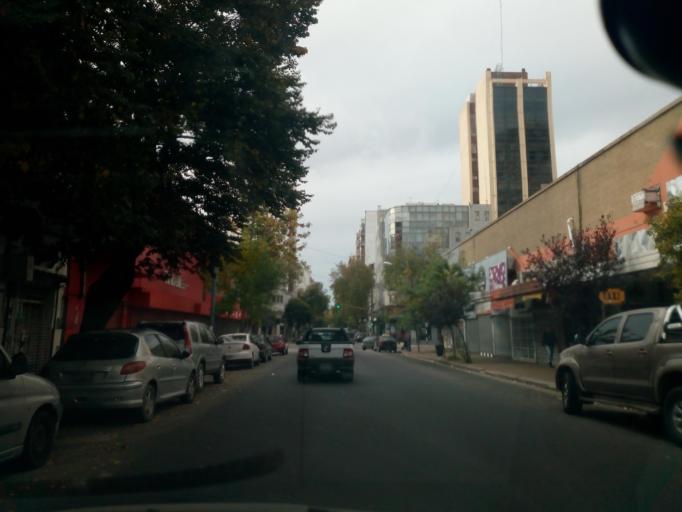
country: AR
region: Buenos Aires
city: Mar del Plata
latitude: -37.9966
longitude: -57.5516
